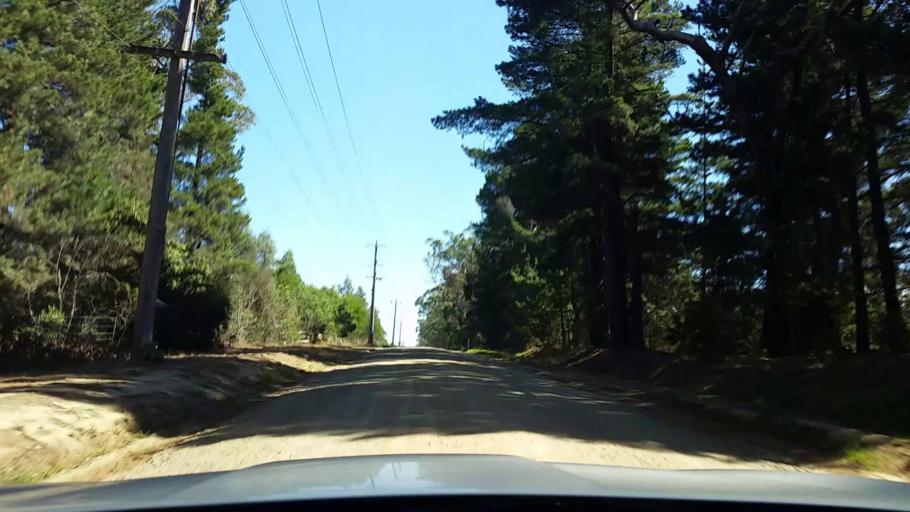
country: AU
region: Victoria
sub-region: Mornington Peninsula
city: Moorooduc
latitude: -38.2802
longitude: 145.1124
